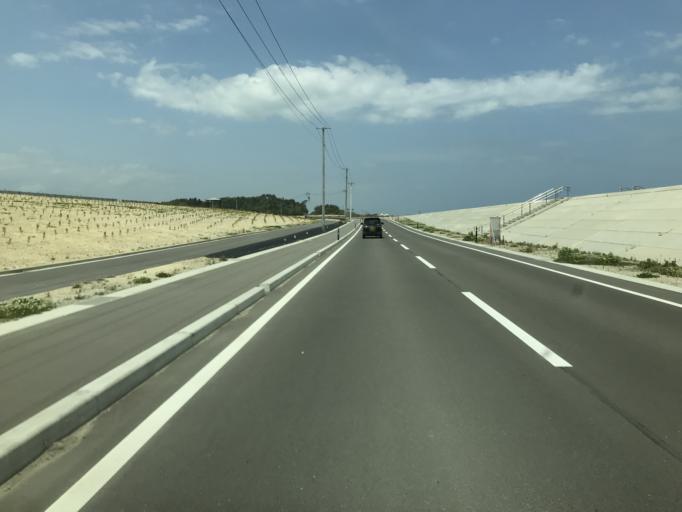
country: JP
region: Miyagi
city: Marumori
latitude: 37.8876
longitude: 140.9319
